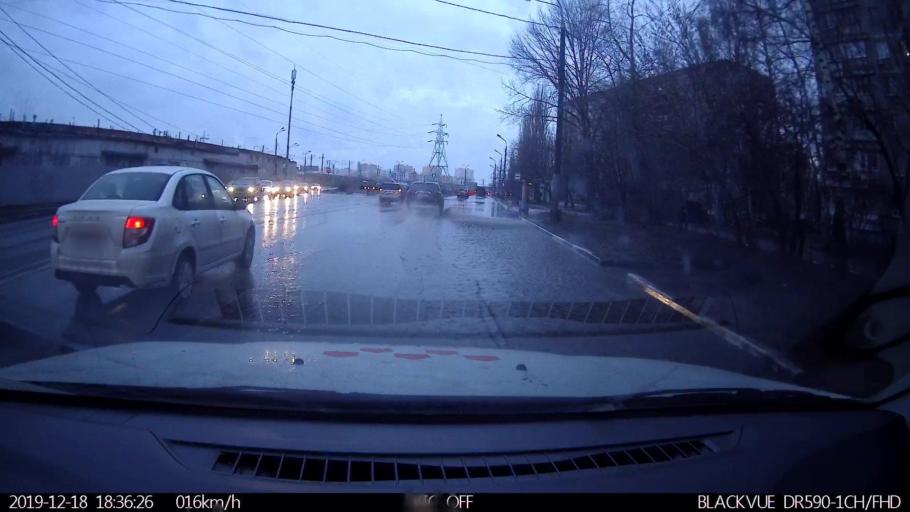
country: RU
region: Nizjnij Novgorod
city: Nizhniy Novgorod
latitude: 56.3364
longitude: 43.9275
